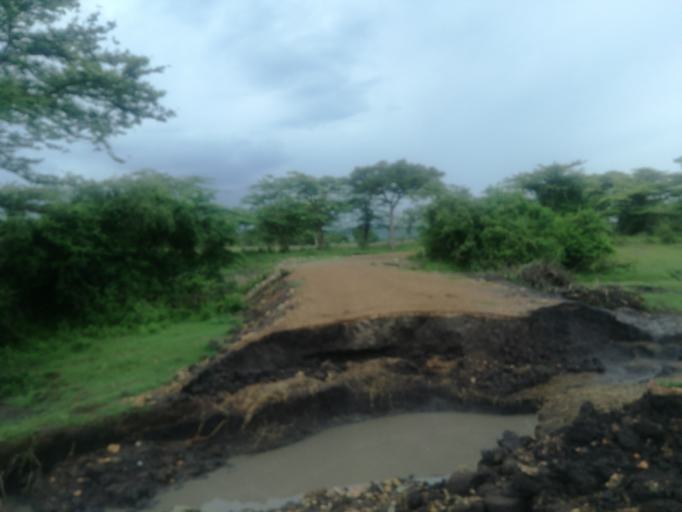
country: TZ
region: Mara
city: Issenye
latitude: -1.9237
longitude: 34.4981
